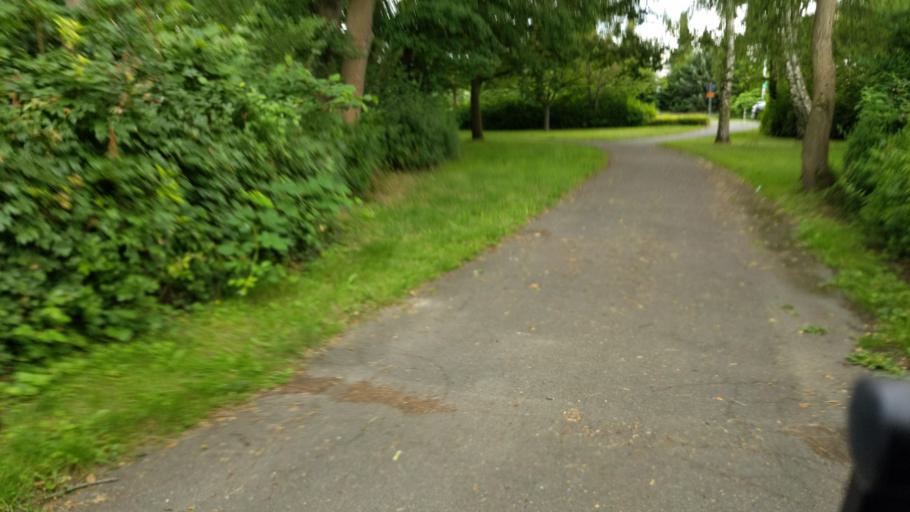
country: DE
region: Lower Saxony
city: Braunschweig
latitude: 52.2344
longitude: 10.5484
